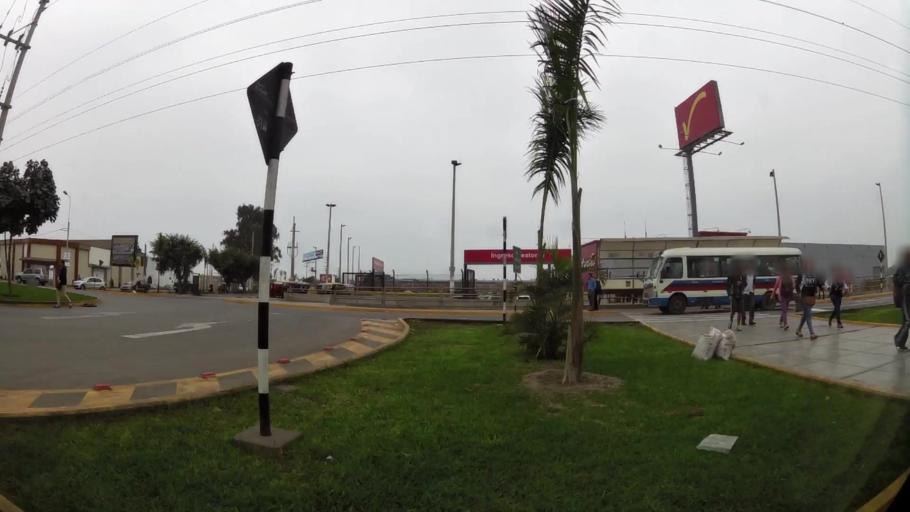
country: PE
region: Lima
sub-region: Lima
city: Punta Hermosa
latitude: -12.2737
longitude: -76.8727
